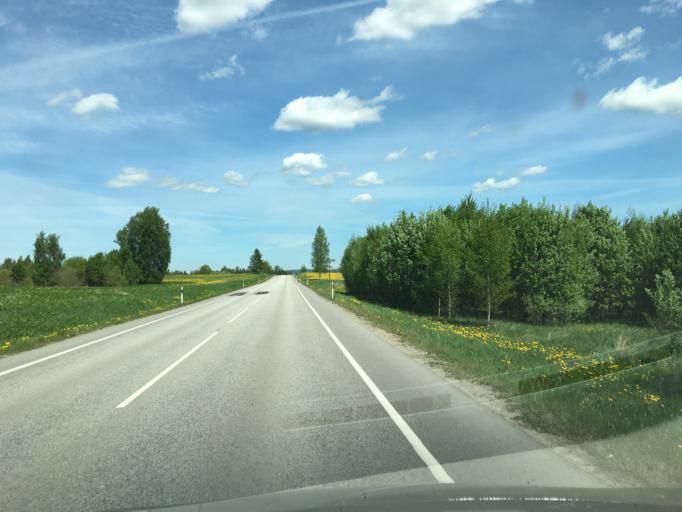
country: EE
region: Vorumaa
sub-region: Antsla vald
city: Vana-Antsla
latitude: 57.8784
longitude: 26.2796
